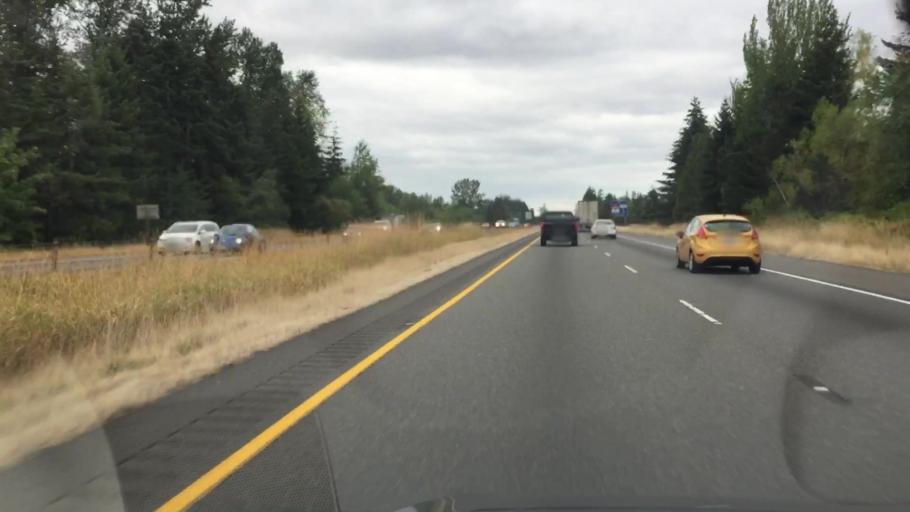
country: US
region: Washington
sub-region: Pierce County
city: Midland
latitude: 47.1583
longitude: -122.3827
